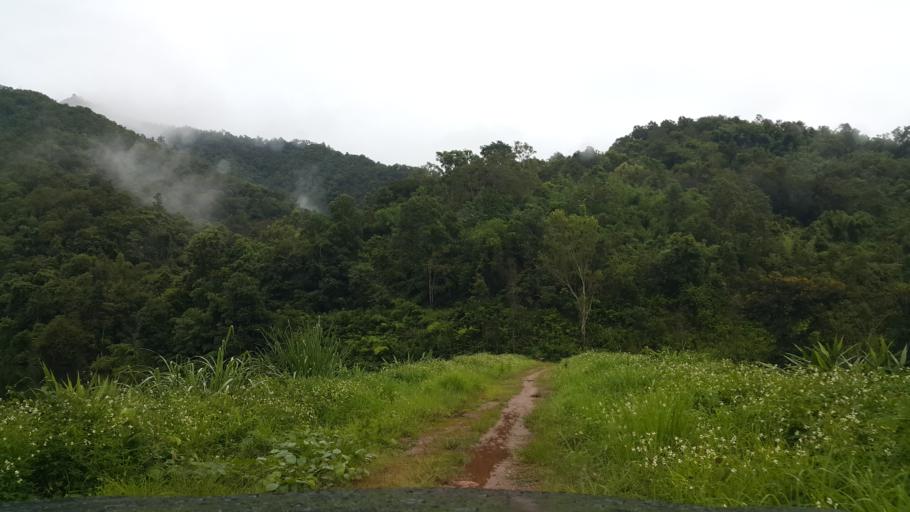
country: TH
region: Phayao
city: Phu Sang
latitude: 19.6259
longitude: 100.4160
